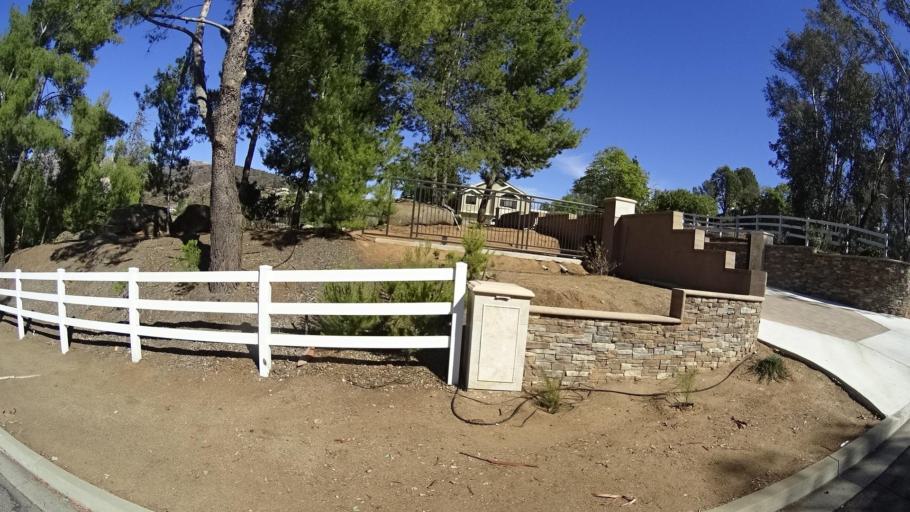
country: US
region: California
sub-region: San Diego County
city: Harbison Canyon
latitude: 32.8682
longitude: -116.8553
